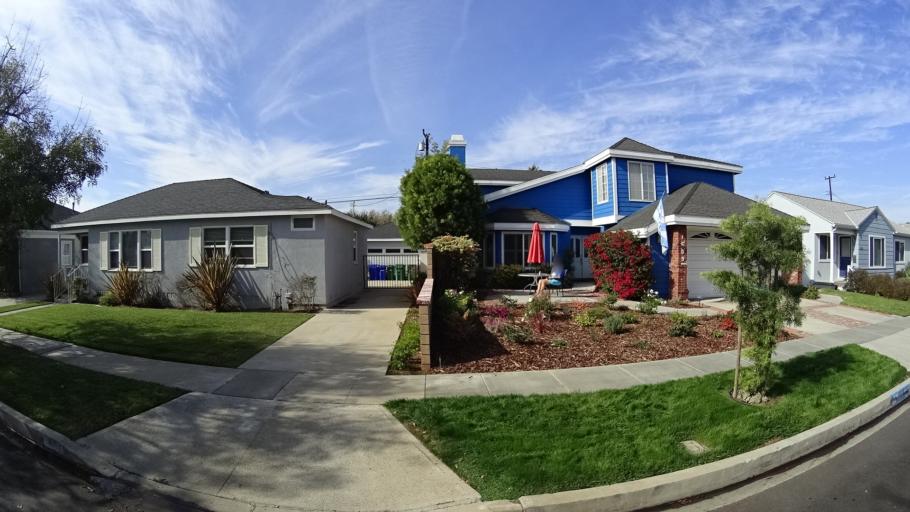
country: US
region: California
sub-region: Los Angeles County
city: Del Aire
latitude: 33.8904
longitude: -118.3809
